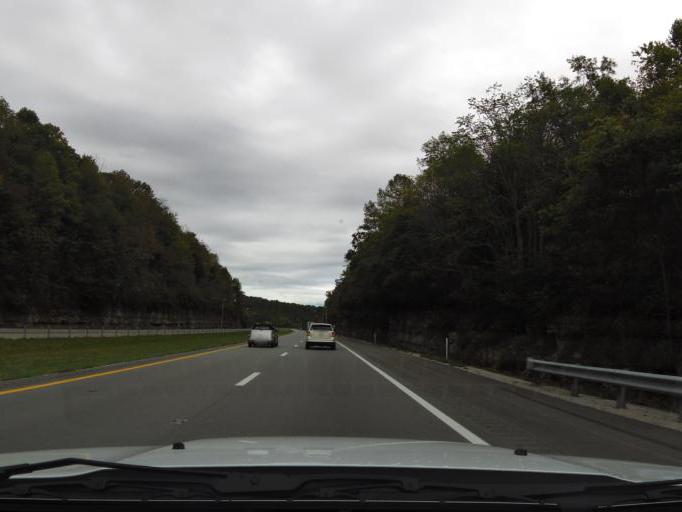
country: US
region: Kentucky
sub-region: Rockcastle County
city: Mount Vernon
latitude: 37.3741
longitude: -84.3234
